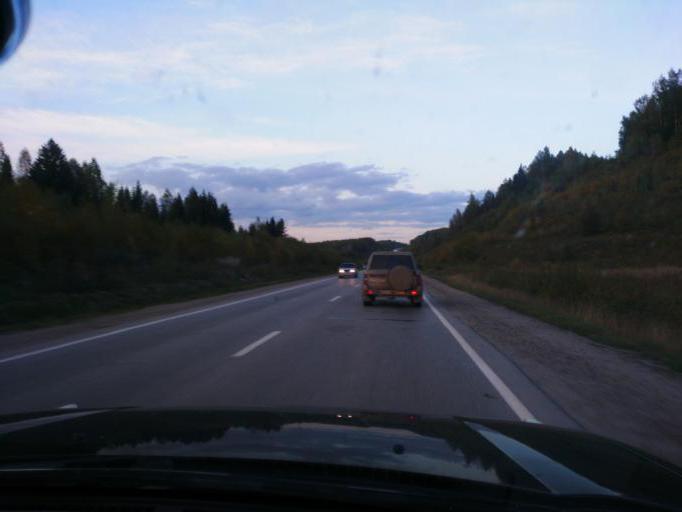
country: RU
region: Perm
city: Polazna
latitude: 58.2930
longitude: 56.5173
